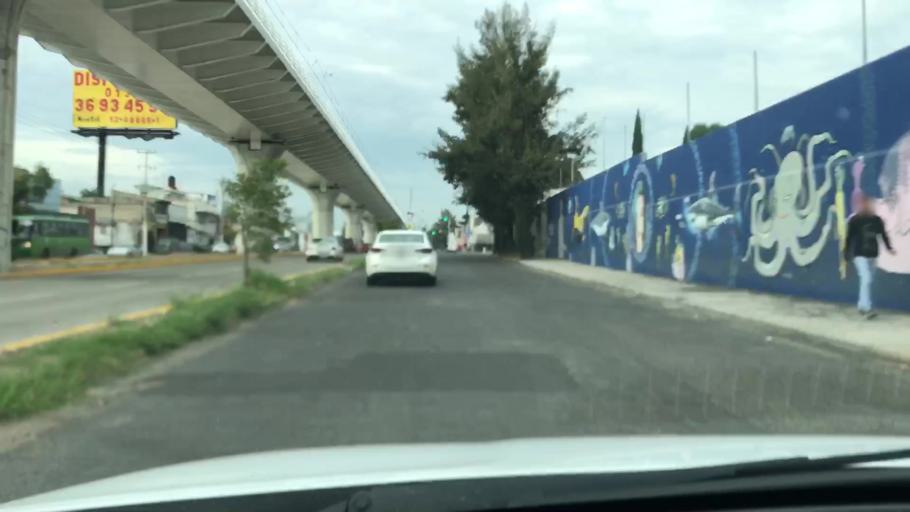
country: MX
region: Jalisco
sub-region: Zapopan
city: Zapopan
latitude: 20.7266
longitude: -103.3868
